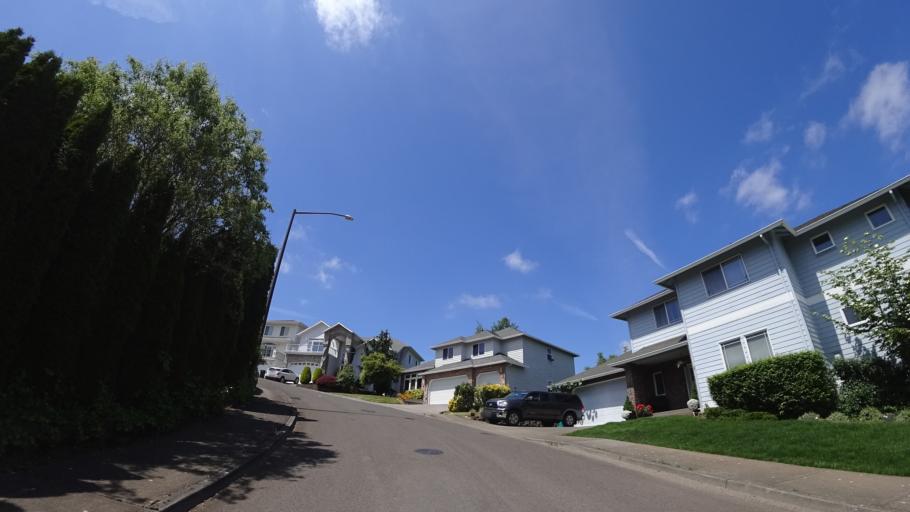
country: US
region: Oregon
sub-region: Clackamas County
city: Happy Valley
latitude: 45.4908
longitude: -122.4939
